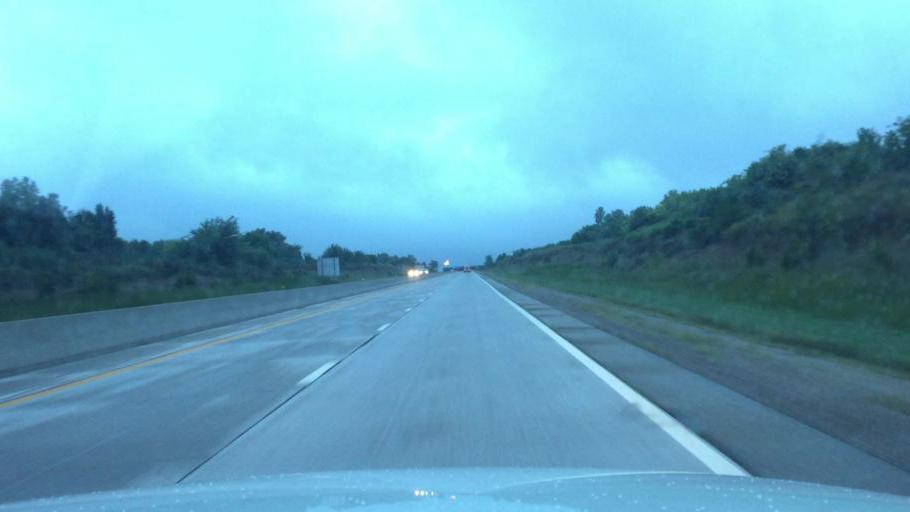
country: US
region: Kansas
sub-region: Neosho County
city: Chanute
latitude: 37.6739
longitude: -95.4795
